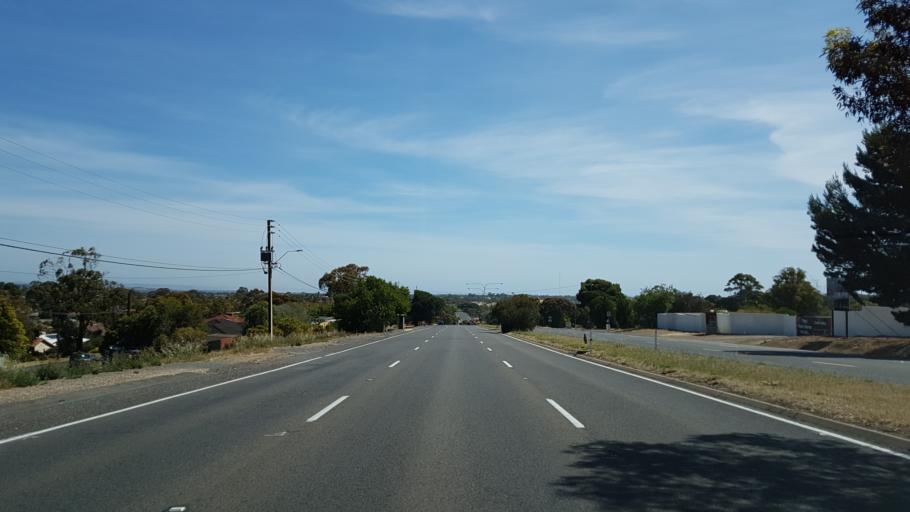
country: AU
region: South Australia
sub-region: Marion
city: Trott Park
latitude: -35.0728
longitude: 138.5527
